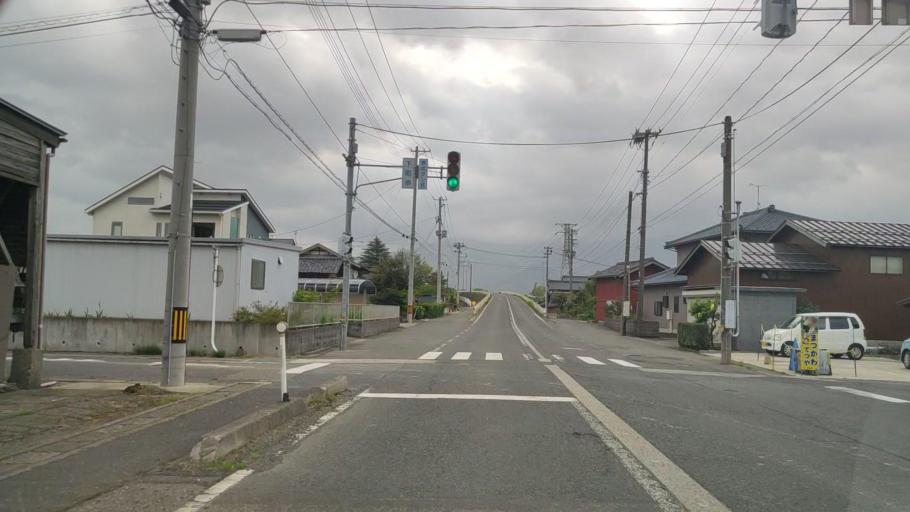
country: JP
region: Niigata
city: Gosen
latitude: 37.7333
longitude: 139.1990
